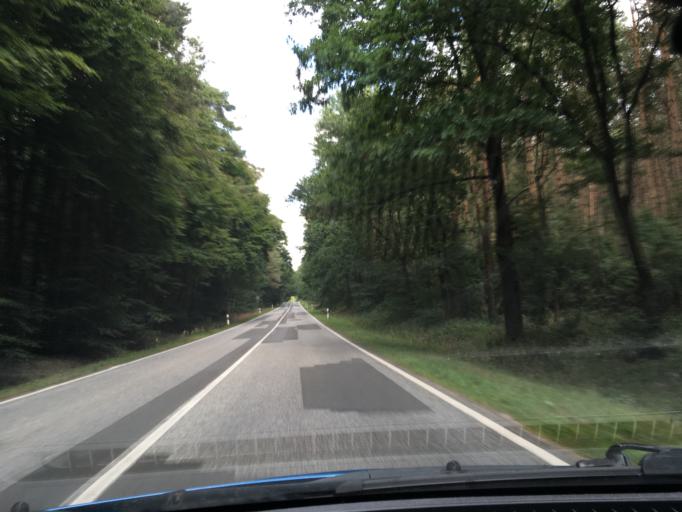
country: DE
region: Mecklenburg-Vorpommern
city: Lubtheen
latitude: 53.3981
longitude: 11.0120
